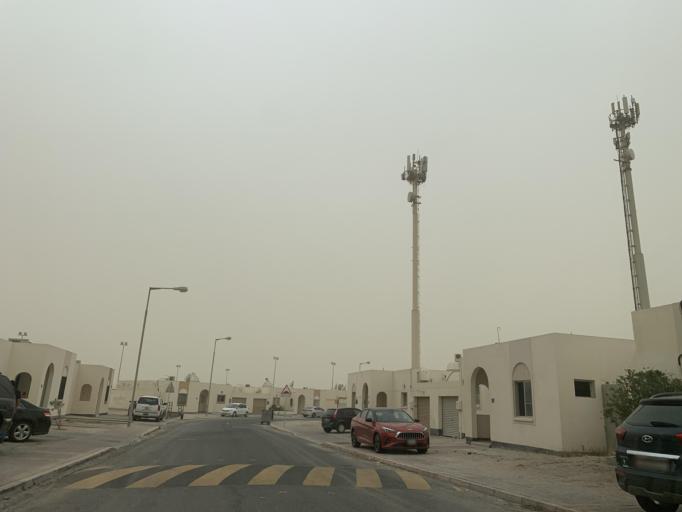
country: BH
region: Central Governorate
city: Madinat Hamad
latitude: 26.1316
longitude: 50.5204
